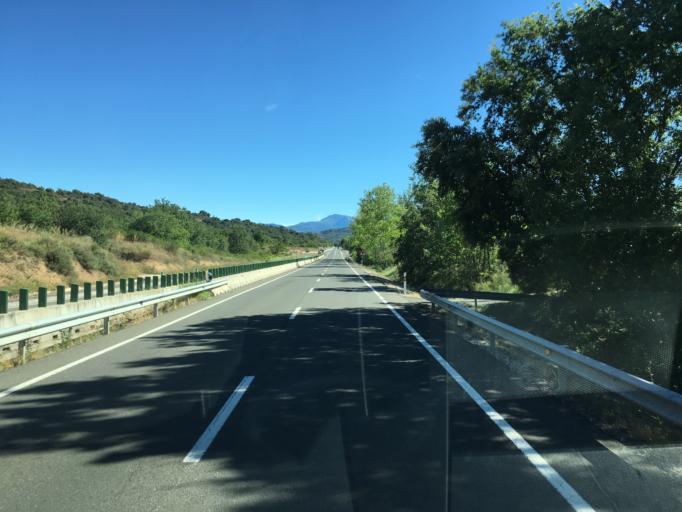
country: ES
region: Aragon
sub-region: Provincia de Huesca
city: Graus
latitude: 42.1449
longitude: 0.3173
